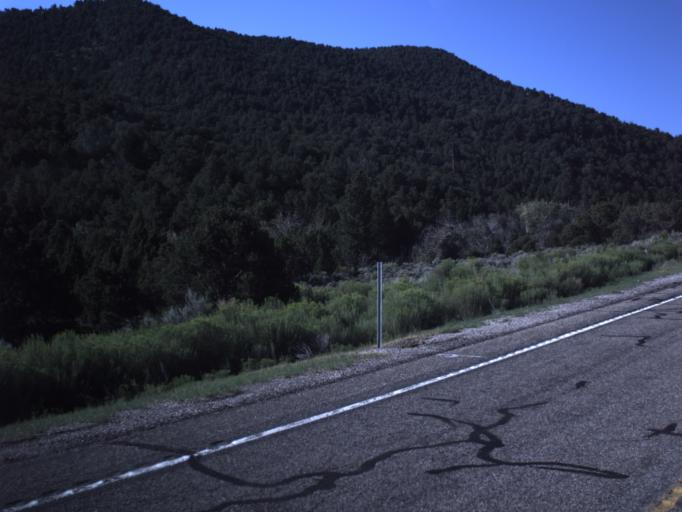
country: US
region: Utah
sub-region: Wayne County
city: Loa
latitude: 38.6686
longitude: -111.4242
